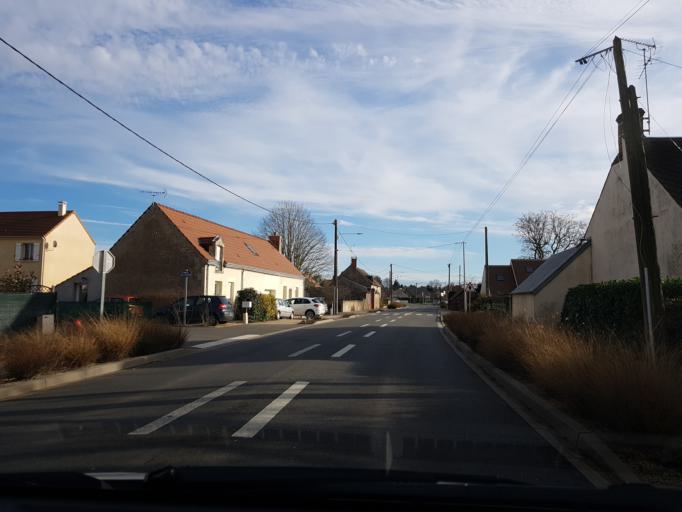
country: FR
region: Centre
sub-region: Departement du Loiret
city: Sandillon
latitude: 47.8490
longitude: 2.0248
